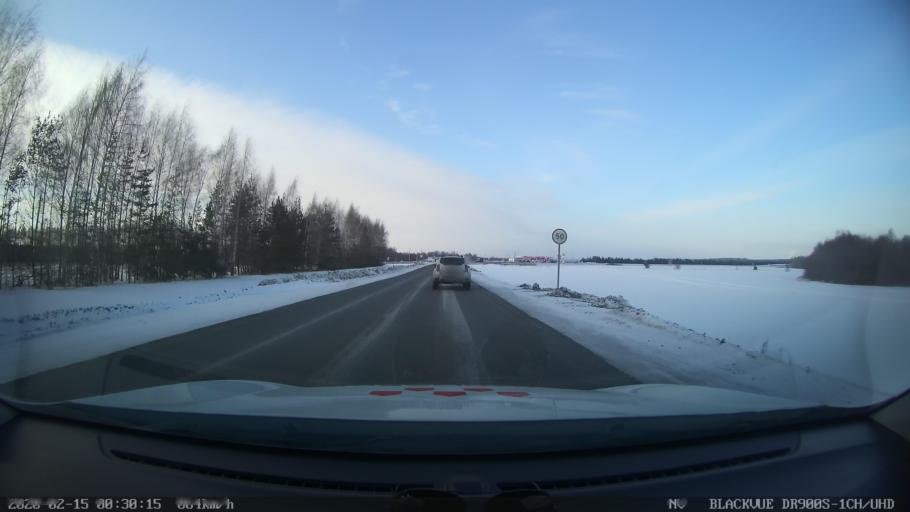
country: RU
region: Tatarstan
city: Verkhniy Uslon
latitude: 55.6576
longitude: 48.8596
